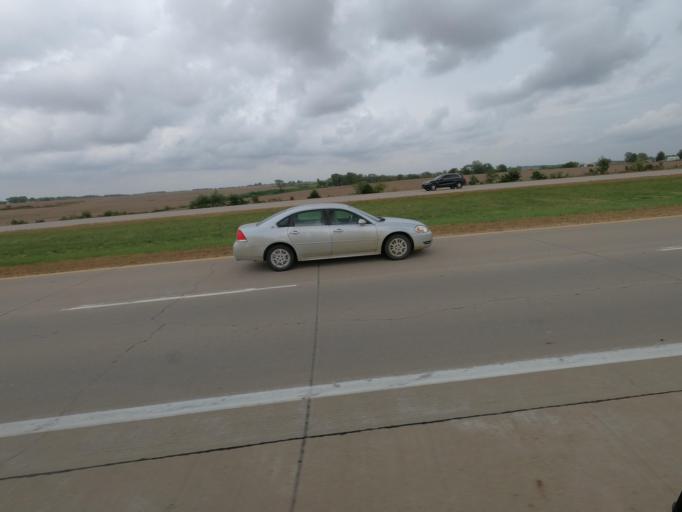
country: US
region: Iowa
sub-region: Wapello County
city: Ottumwa
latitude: 41.0002
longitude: -92.2438
